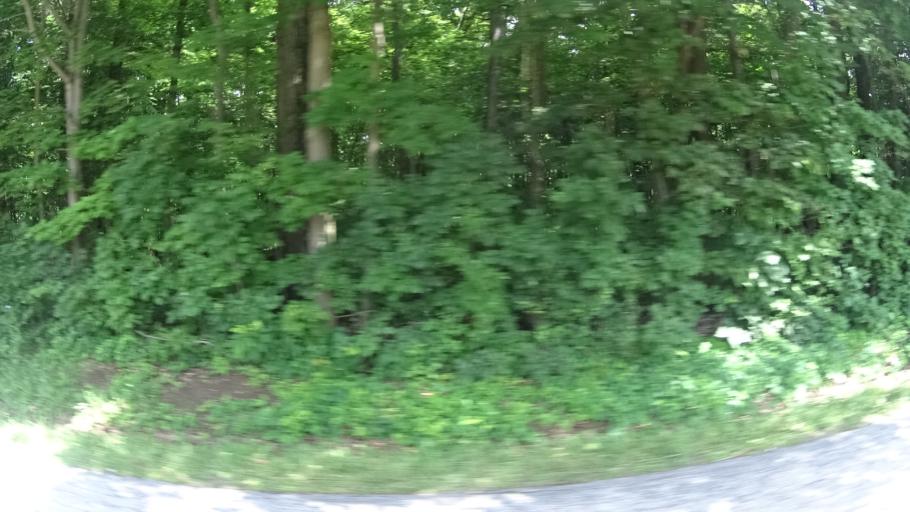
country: US
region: Ohio
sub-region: Huron County
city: Wakeman
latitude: 41.3197
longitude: -82.3712
